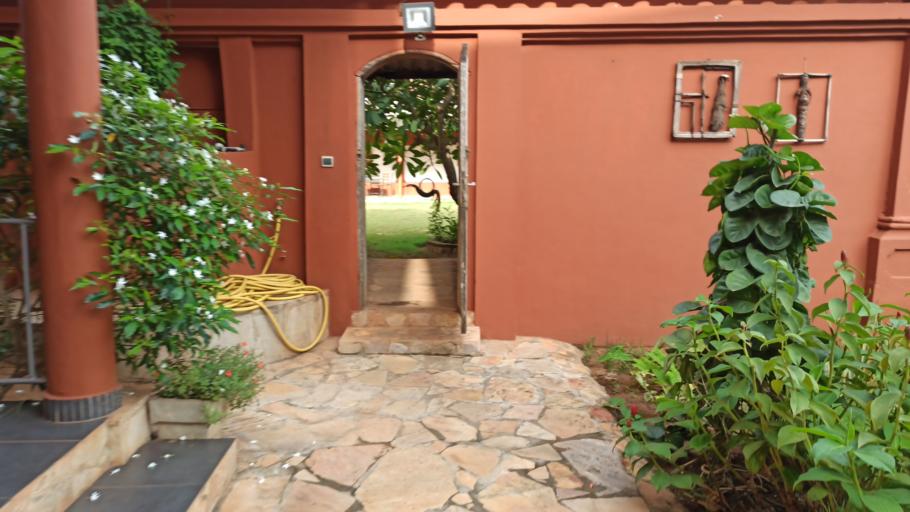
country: BJ
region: Queme
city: Porto-Novo
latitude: 6.5007
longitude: 2.6081
